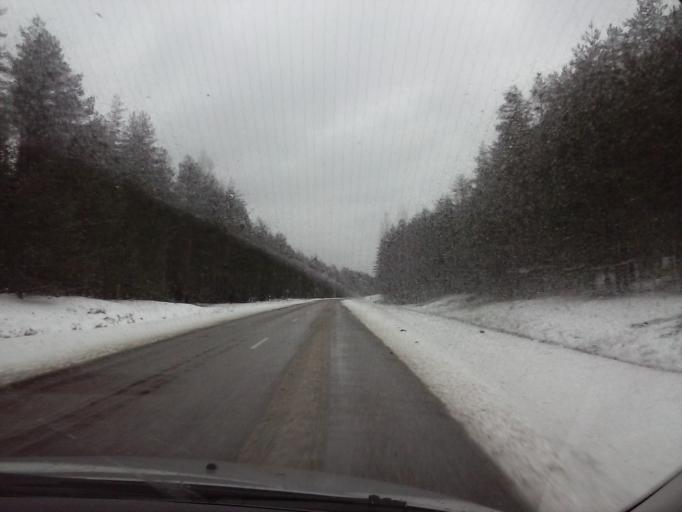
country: LV
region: Strenci
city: Seda
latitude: 57.6644
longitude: 25.8743
